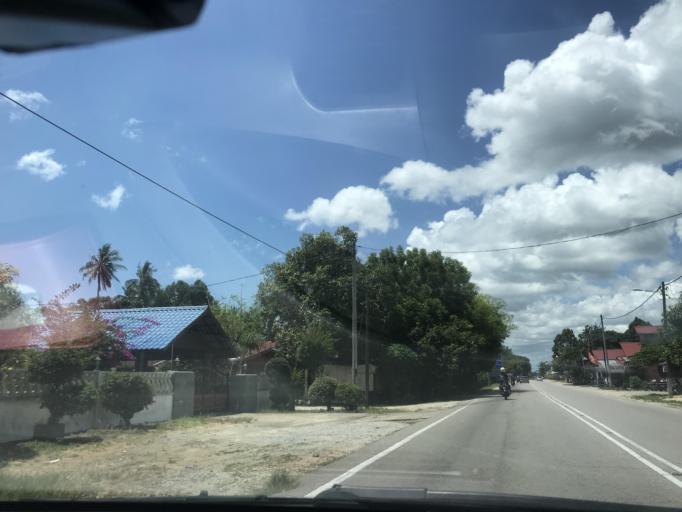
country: MY
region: Kelantan
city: Tumpat
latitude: 6.1931
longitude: 102.1498
